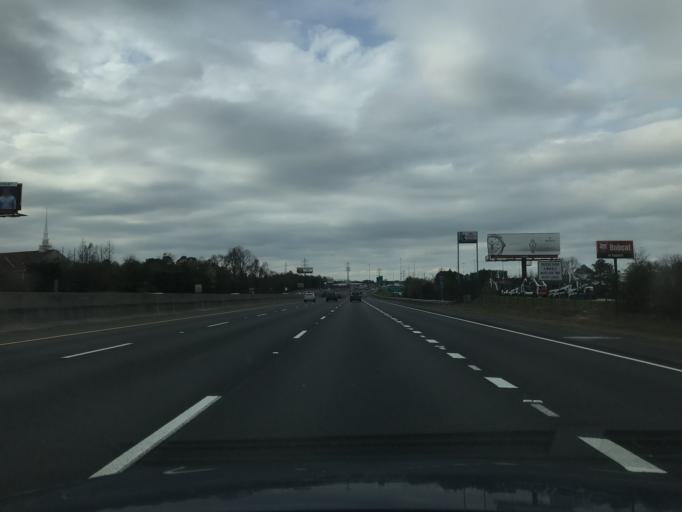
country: US
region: Georgia
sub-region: Columbia County
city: Martinez
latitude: 33.4584
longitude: -82.0780
